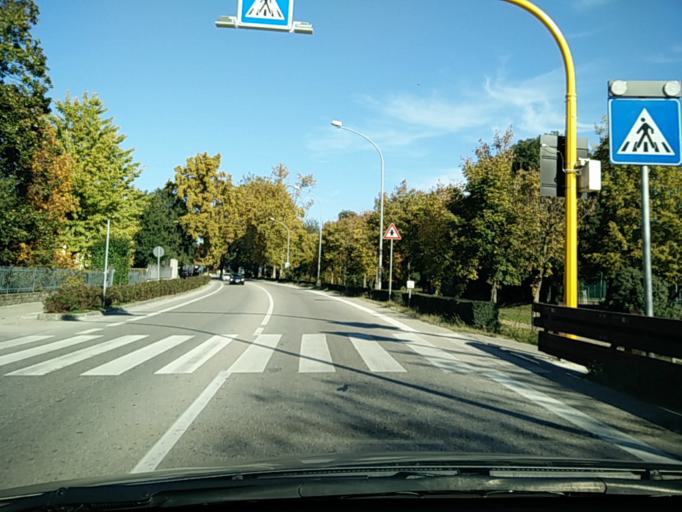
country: IT
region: Veneto
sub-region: Provincia di Treviso
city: Spresiano
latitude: 45.7769
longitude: 12.2590
